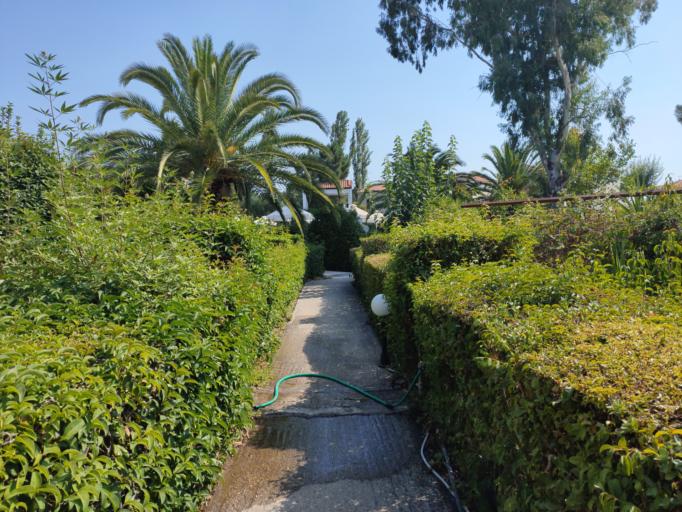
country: GR
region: North Aegean
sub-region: Nomos Lesvou
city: Kalloni
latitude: 39.2096
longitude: 26.2059
